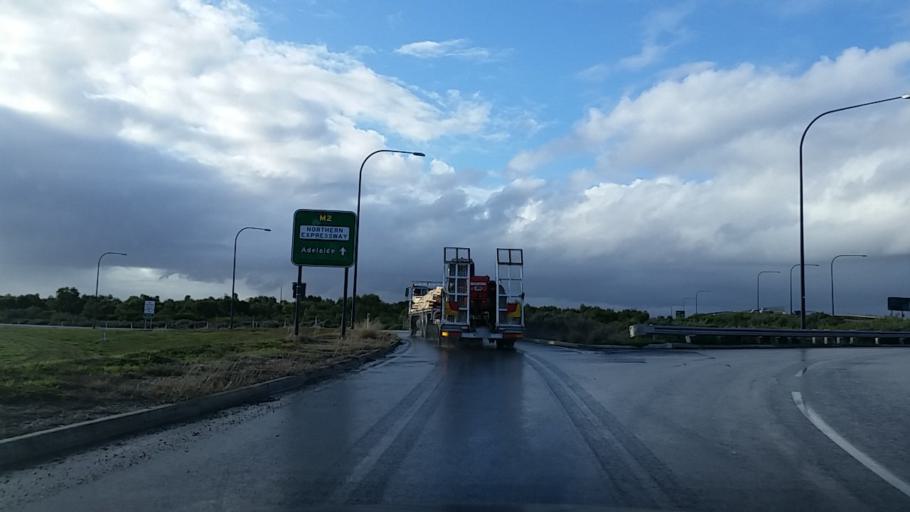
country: AU
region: South Australia
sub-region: Playford
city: Angle Vale
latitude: -34.6813
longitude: 138.6215
